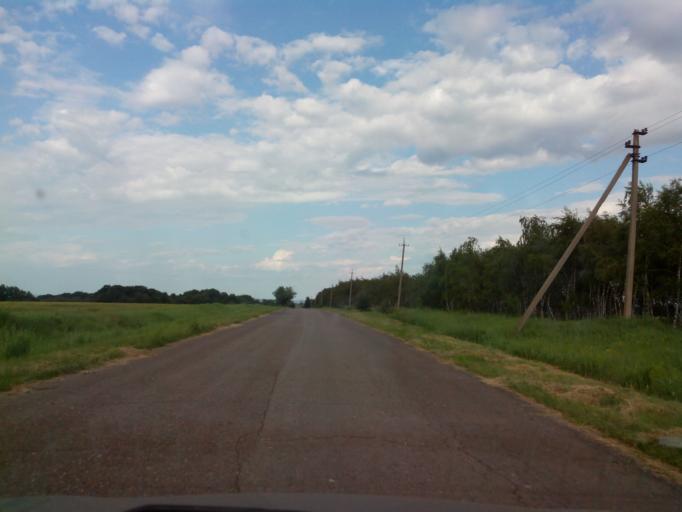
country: RU
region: Volgograd
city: Slashchevskaya
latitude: 49.7943
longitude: 42.3900
